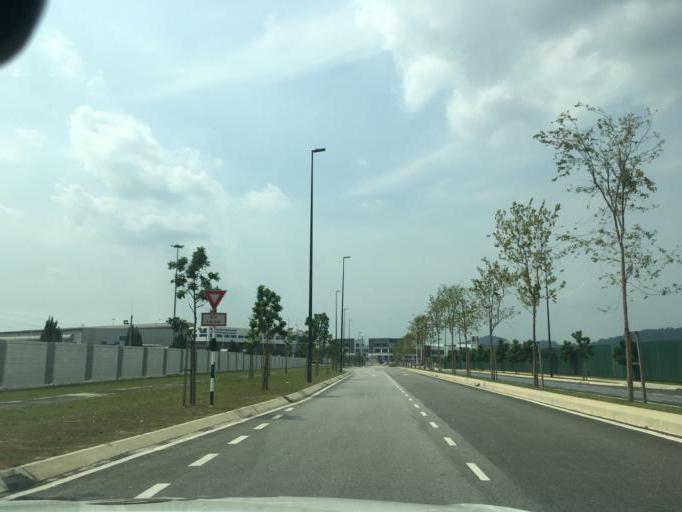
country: MY
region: Selangor
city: Klang
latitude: 3.0824
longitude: 101.4765
